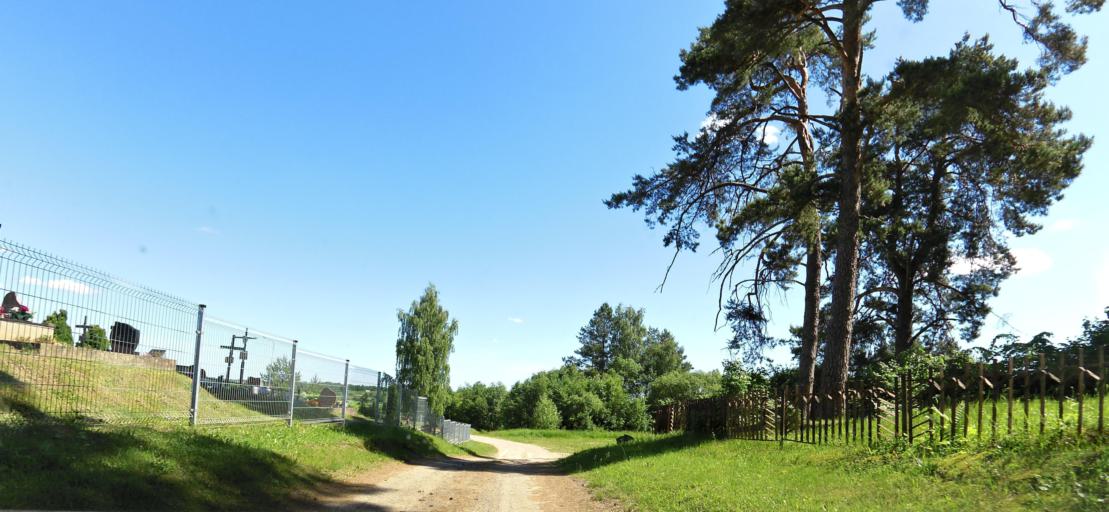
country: LT
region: Vilnius County
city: Pasilaiciai
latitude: 54.9513
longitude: 25.2381
